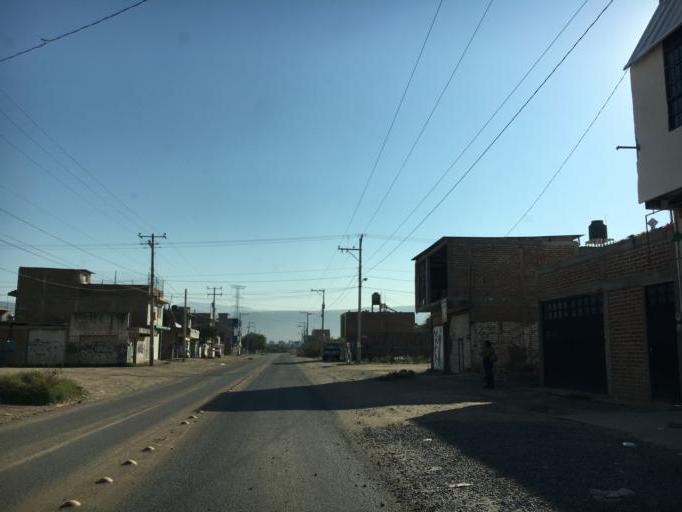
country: MX
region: Guanajuato
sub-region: Leon
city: Fraccionamiento Paraiso Real
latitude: 21.1016
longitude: -101.6003
